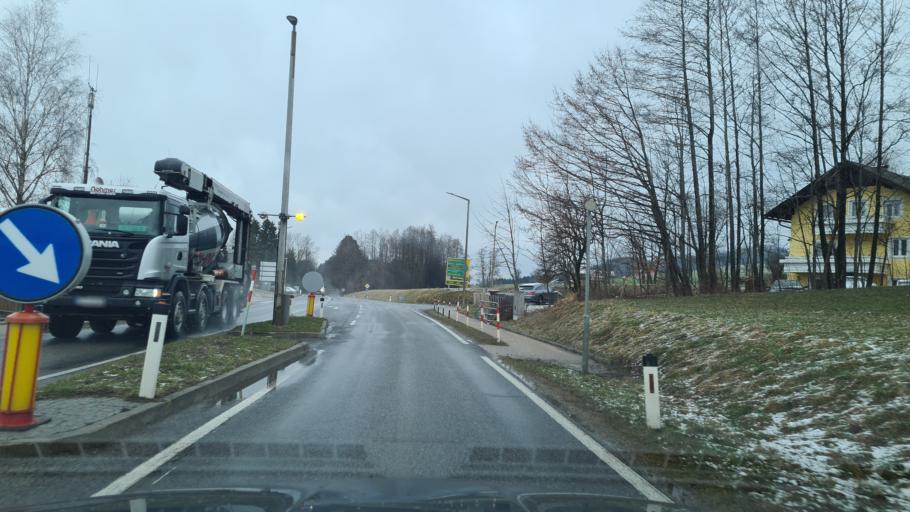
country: AT
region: Upper Austria
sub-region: Politischer Bezirk Vocklabruck
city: Zell am Moos
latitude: 47.9031
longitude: 13.3211
